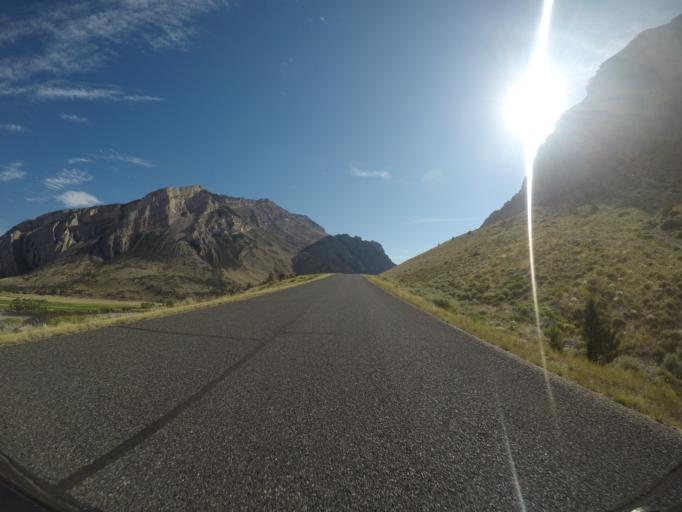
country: US
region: Montana
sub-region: Carbon County
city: Red Lodge
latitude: 44.8543
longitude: -109.2964
